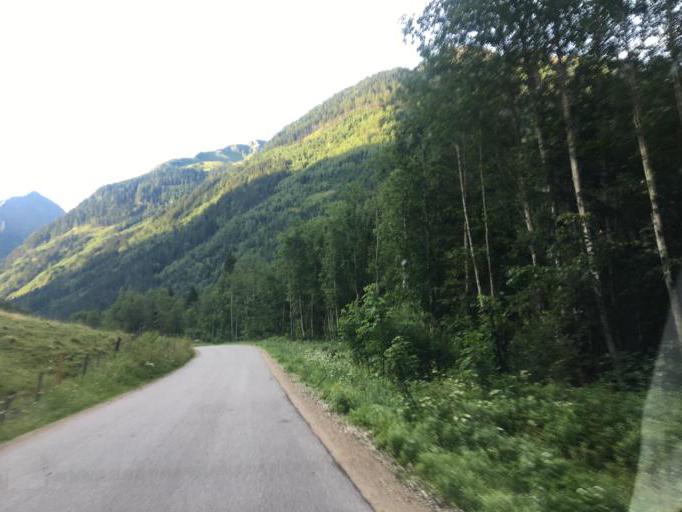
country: AT
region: Styria
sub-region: Politischer Bezirk Liezen
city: Haus
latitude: 47.3393
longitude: 13.7417
